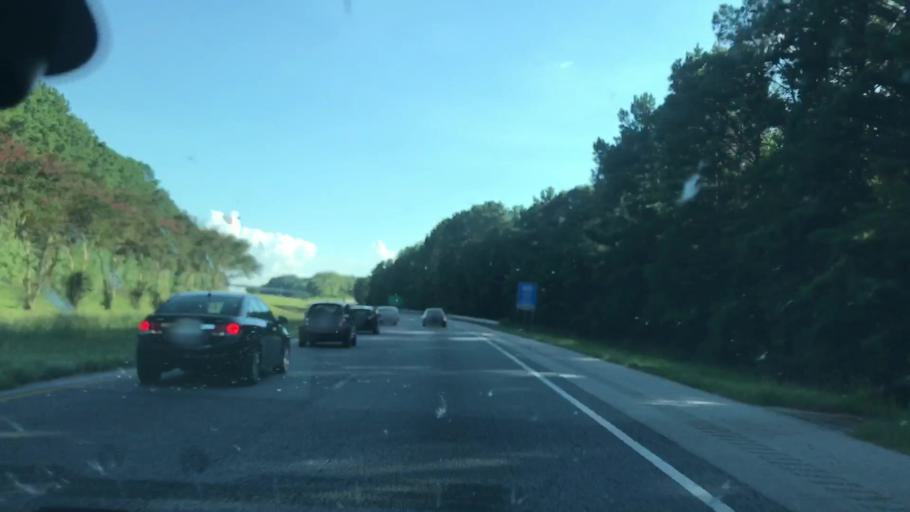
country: US
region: Alabama
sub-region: Chambers County
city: Valley
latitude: 32.8211
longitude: -85.0208
